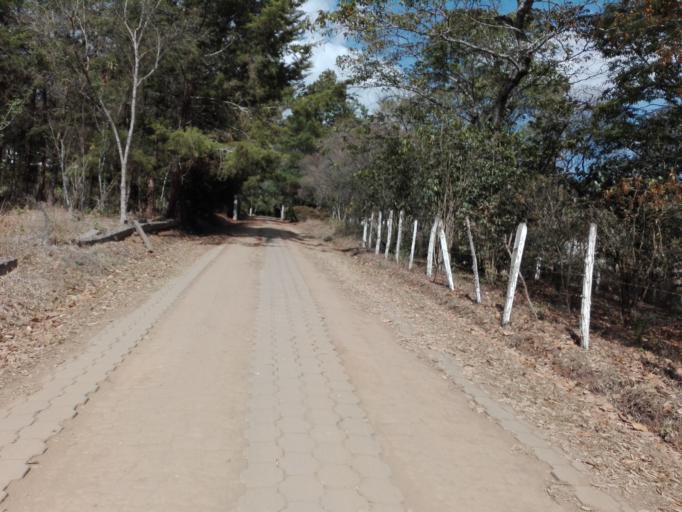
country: GT
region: Sacatepequez
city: Santo Domingo Xenacoj
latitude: 14.6859
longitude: -90.7025
